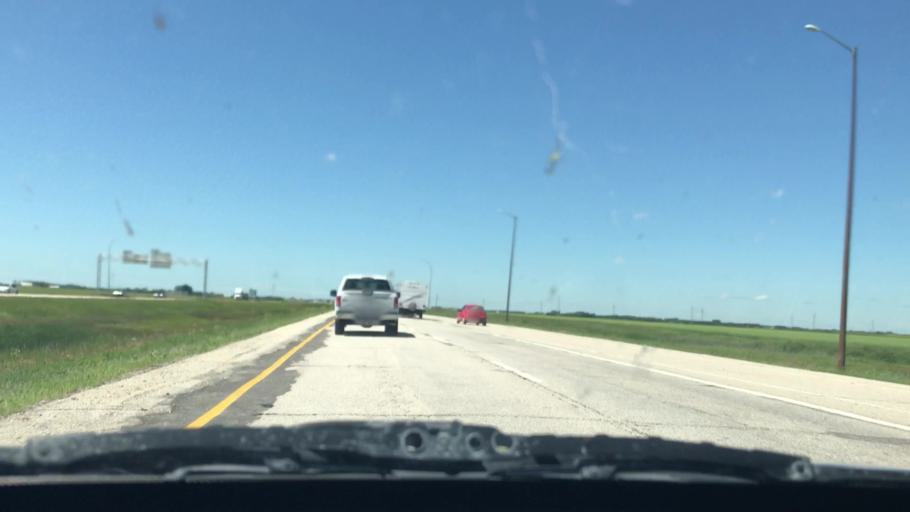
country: CA
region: Manitoba
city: Steinbach
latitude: 49.7035
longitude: -96.6519
